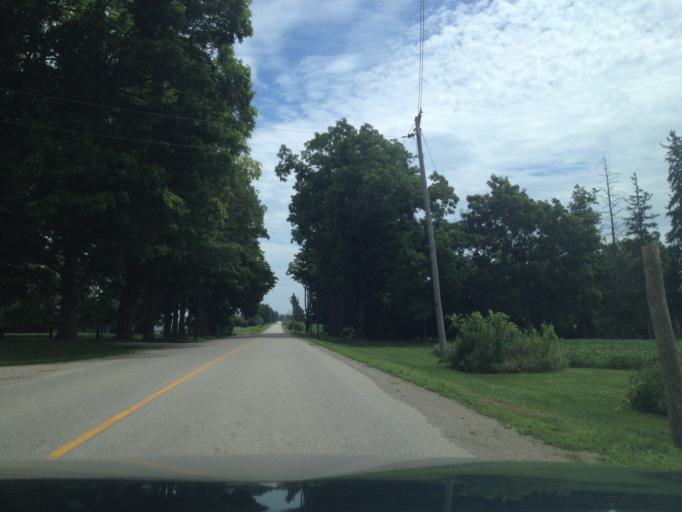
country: CA
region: Ontario
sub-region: Oxford County
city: Woodstock
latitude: 42.9918
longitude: -80.6672
